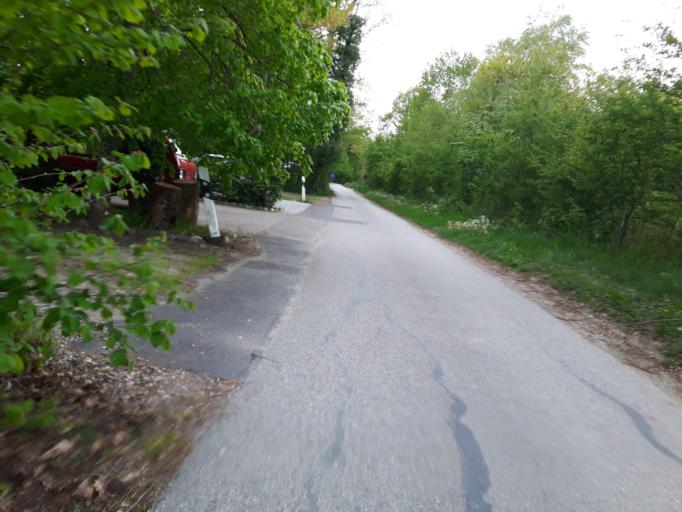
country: CH
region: Vaud
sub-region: Jura-Nord vaudois District
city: Grandson
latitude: 46.8142
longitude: 6.6562
